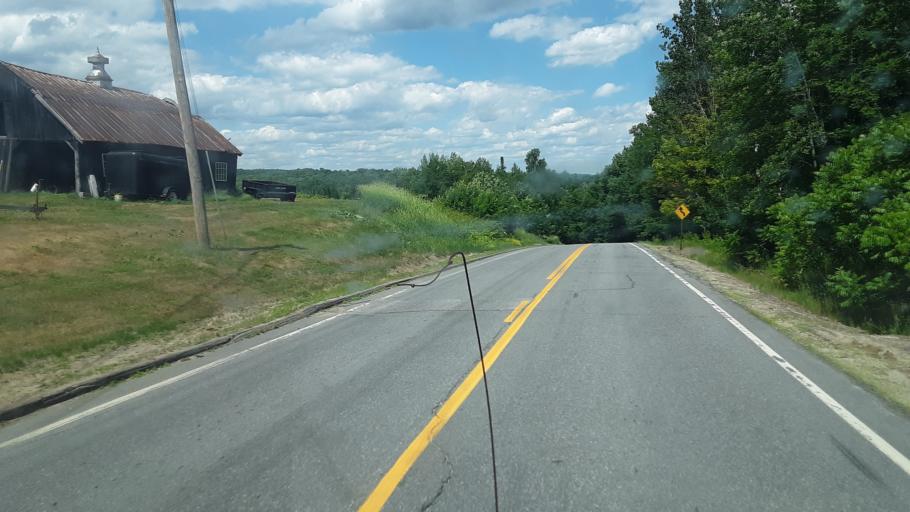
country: US
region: Maine
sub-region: Franklin County
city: Chesterville
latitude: 44.5839
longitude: -70.1524
